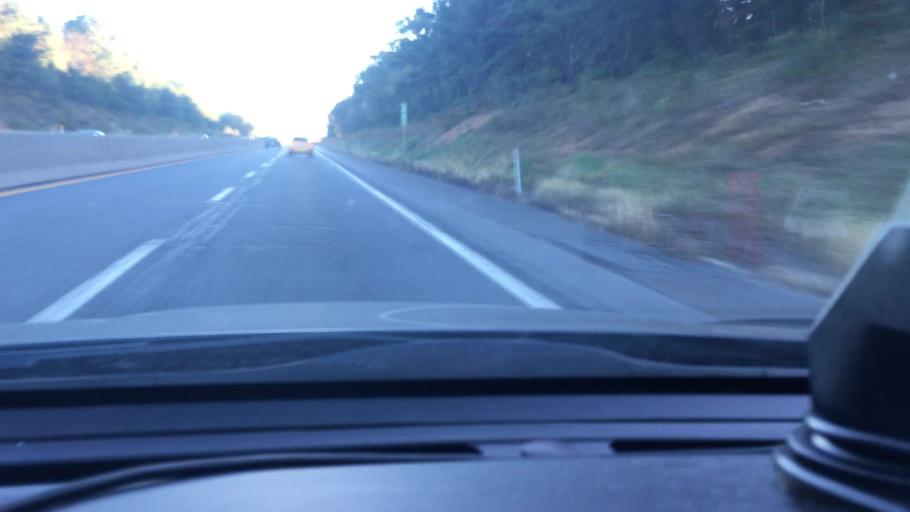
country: US
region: Pennsylvania
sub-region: Carbon County
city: Towamensing Trails
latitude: 40.9439
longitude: -75.6380
